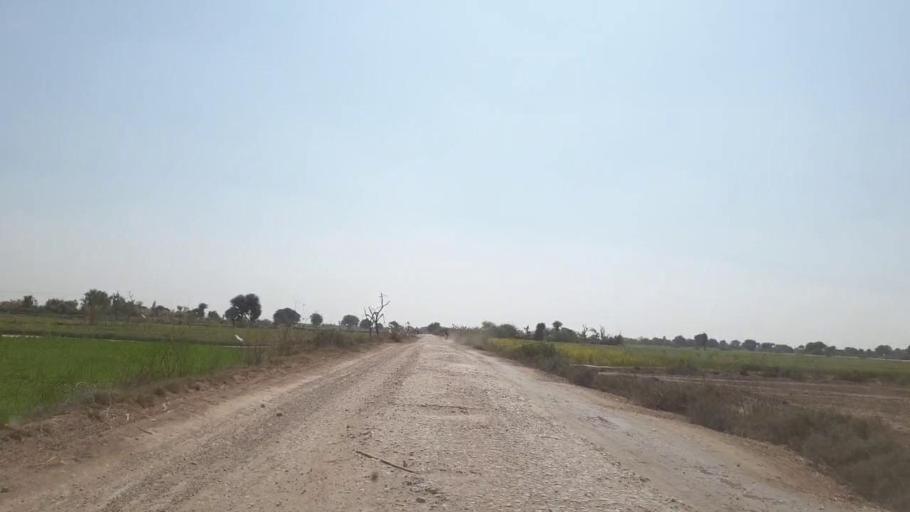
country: PK
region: Sindh
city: Mirpur Khas
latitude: 25.7399
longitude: 69.0823
